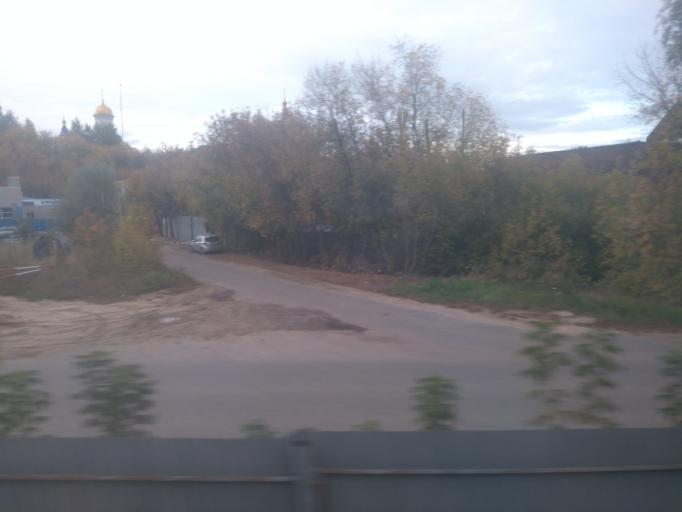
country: RU
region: Tatarstan
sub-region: Gorod Kazan'
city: Kazan
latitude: 55.8054
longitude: 49.0570
